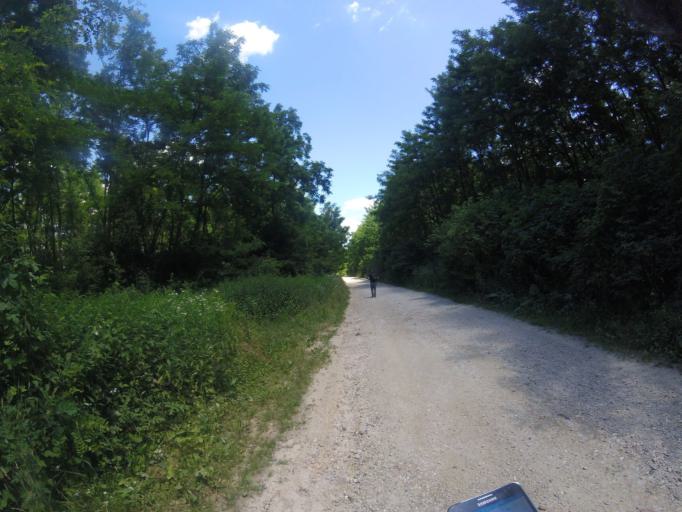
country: HU
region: Zala
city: Zalalovo
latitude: 46.8372
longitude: 16.5712
